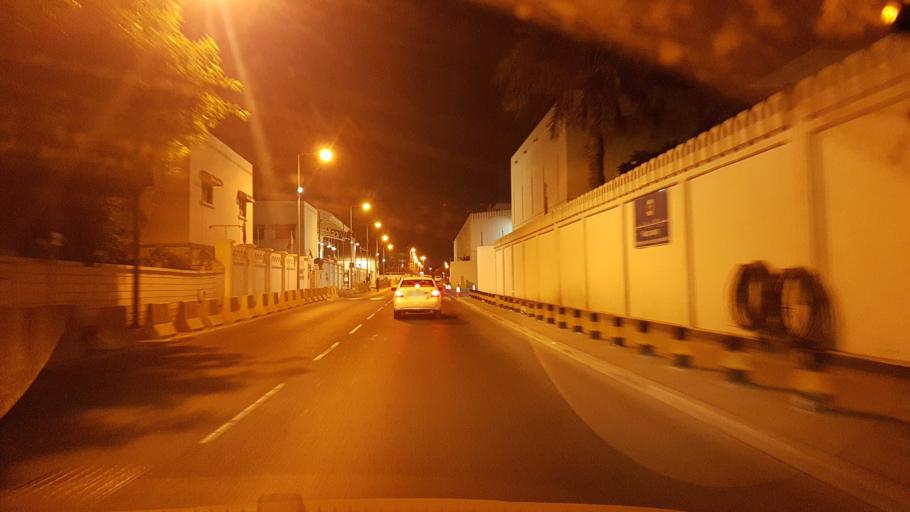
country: BH
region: Manama
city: Manama
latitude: 26.2242
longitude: 50.5775
